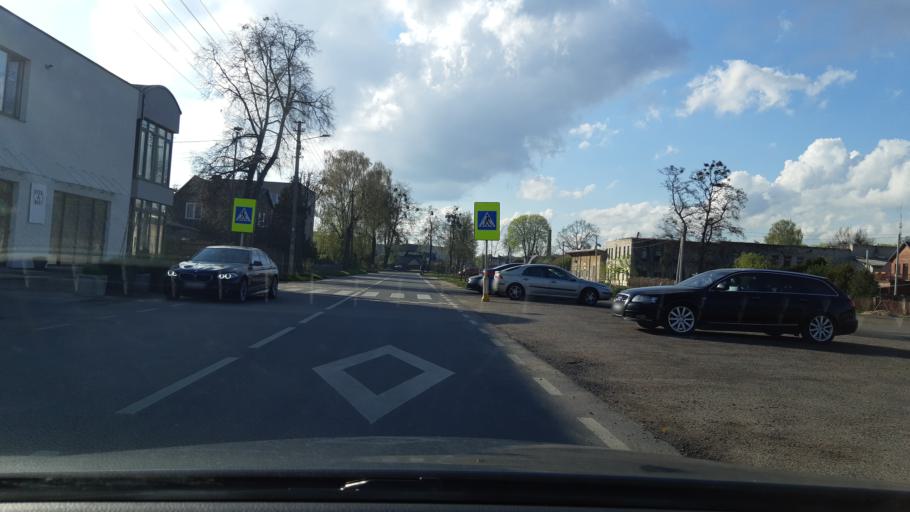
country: LT
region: Kauno apskritis
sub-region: Kaunas
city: Aleksotas
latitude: 54.8718
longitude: 23.9424
